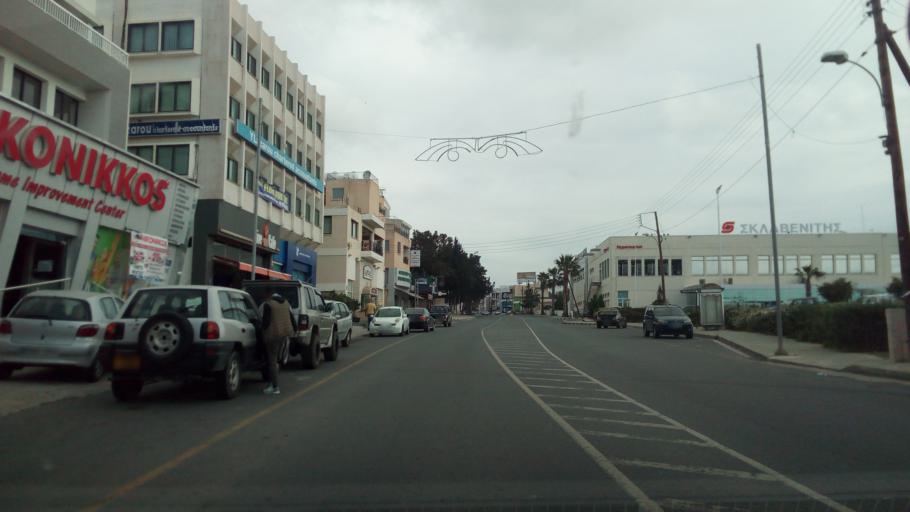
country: CY
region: Pafos
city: Paphos
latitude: 34.7877
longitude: 32.4333
